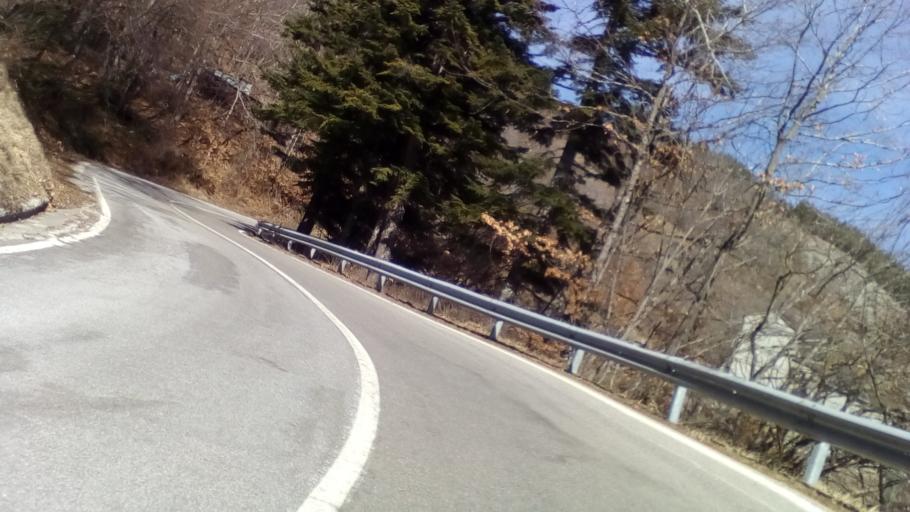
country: IT
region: Emilia-Romagna
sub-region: Provincia di Modena
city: Pievepelago
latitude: 44.2205
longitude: 10.6232
